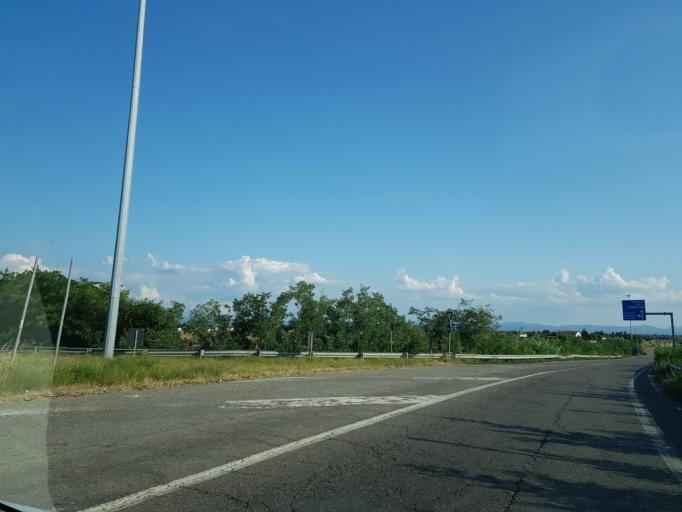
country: IT
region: Piedmont
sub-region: Provincia di Alessandria
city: Litta Parodi-Cascinagrossa
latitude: 44.8820
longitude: 8.6978
